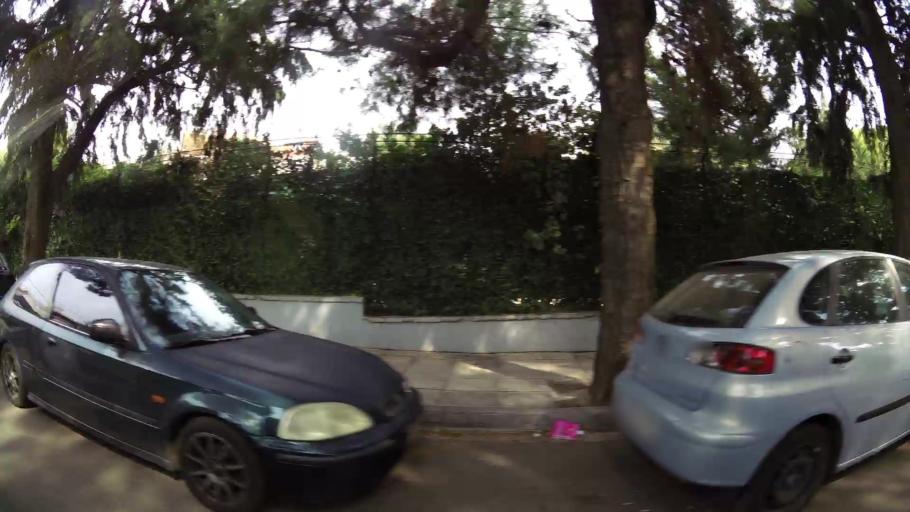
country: GR
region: Attica
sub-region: Nomarchia Athinas
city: Neo Psychiko
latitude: 38.0139
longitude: 23.7808
